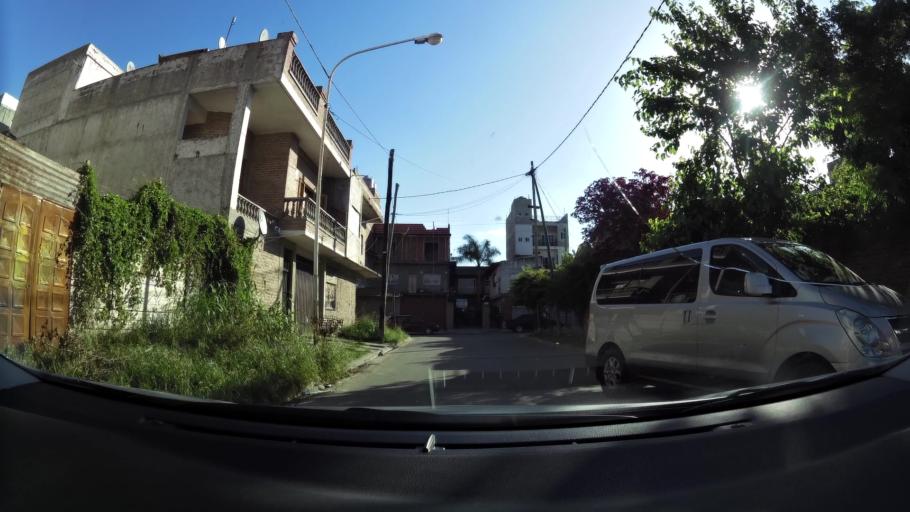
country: AR
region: Buenos Aires F.D.
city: Villa Lugano
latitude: -34.7030
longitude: -58.4778
